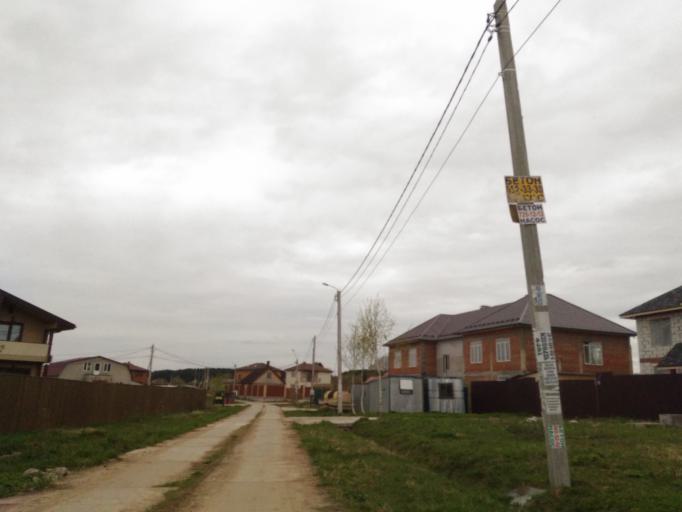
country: RU
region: Moskovskaya
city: Dedovsk
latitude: 55.8524
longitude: 37.1352
